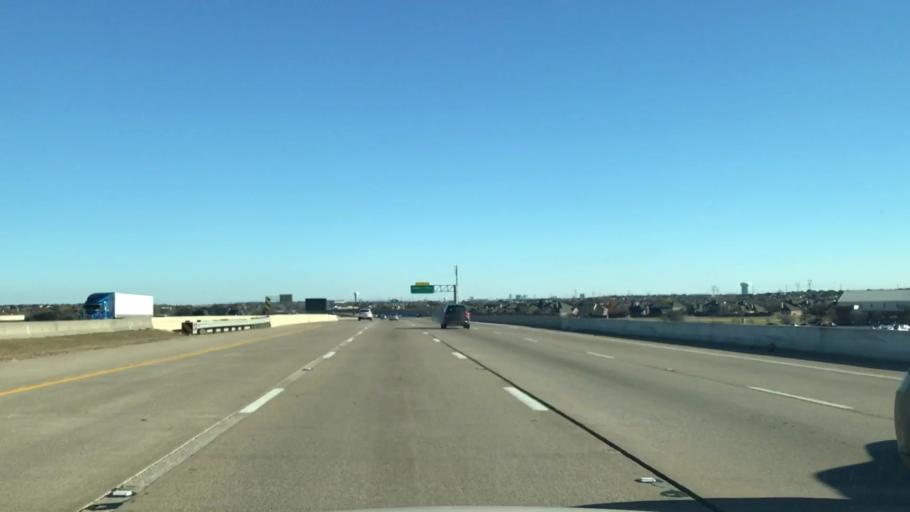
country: US
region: Texas
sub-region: Denton County
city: Lewisville
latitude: 33.0114
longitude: -96.9438
